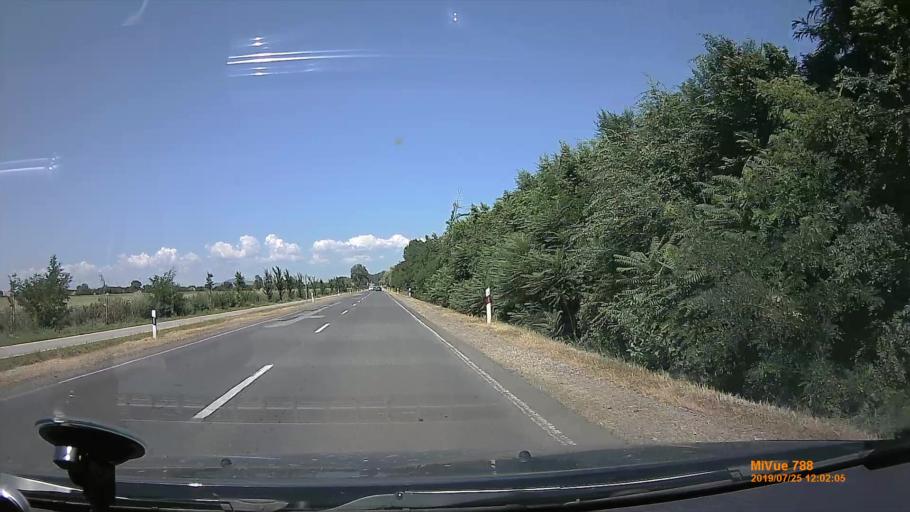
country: HU
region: Szabolcs-Szatmar-Bereg
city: Nyirtelek
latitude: 48.0492
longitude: 21.5703
